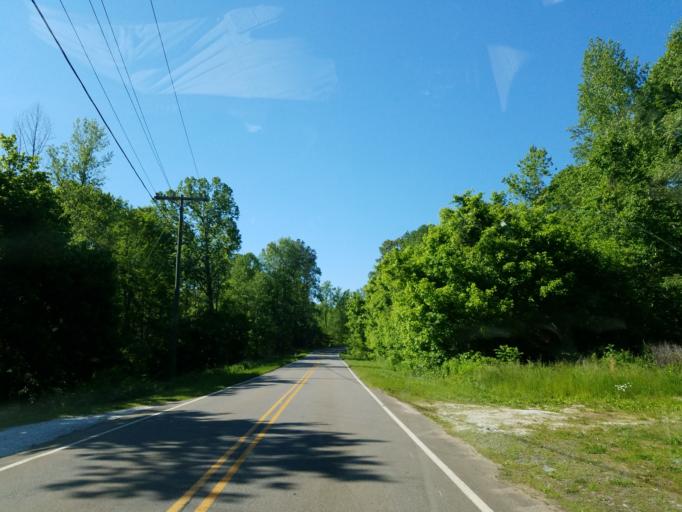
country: US
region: Georgia
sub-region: Pickens County
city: Jasper
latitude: 34.5229
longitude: -84.5094
